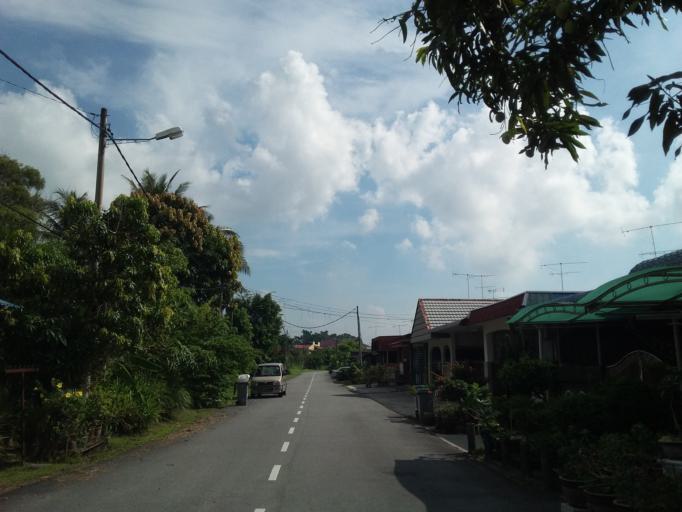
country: MY
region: Johor
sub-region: Daerah Batu Pahat
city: Batu Pahat
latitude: 1.8396
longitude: 102.9252
